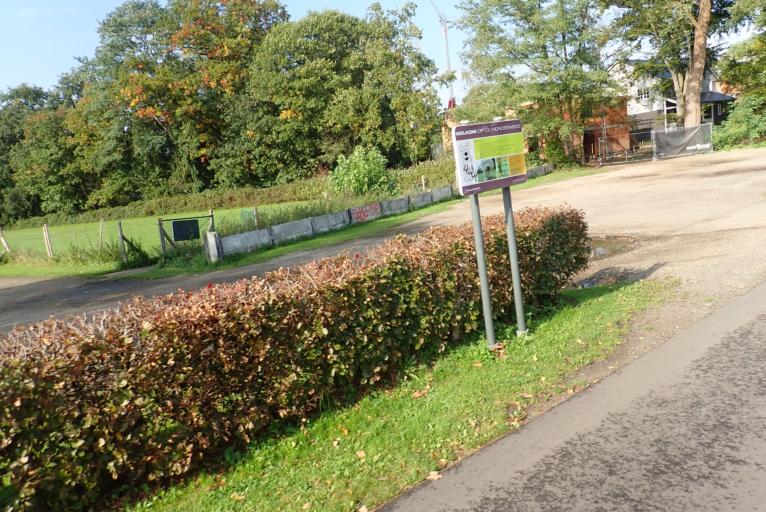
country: BE
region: Flanders
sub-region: Provincie Antwerpen
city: Kalmthout
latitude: 51.3955
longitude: 4.4663
